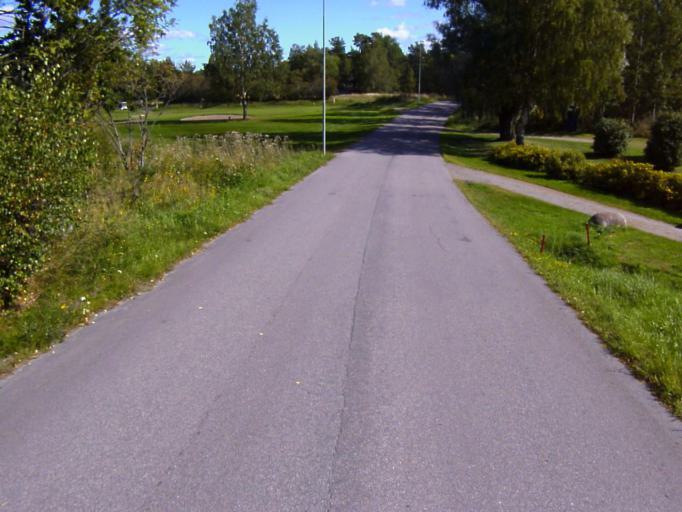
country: SE
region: Soedermanland
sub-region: Eskilstuna Kommun
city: Eskilstuna
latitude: 59.3611
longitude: 16.5486
